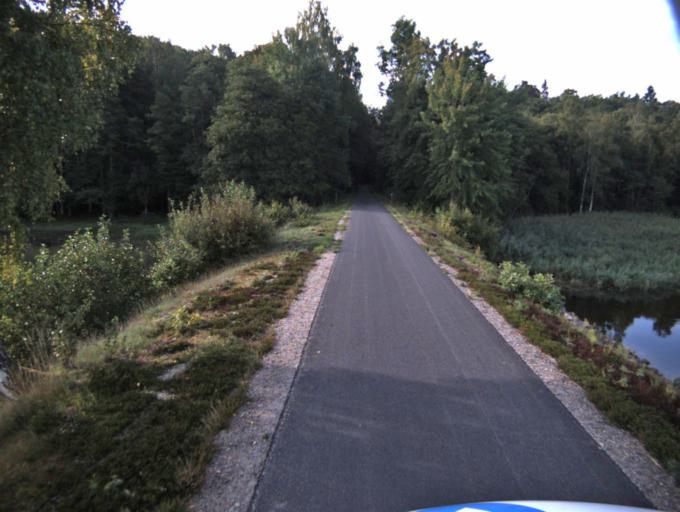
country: SE
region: Vaestra Goetaland
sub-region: Ulricehamns Kommun
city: Ulricehamn
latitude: 57.7307
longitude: 13.4097
